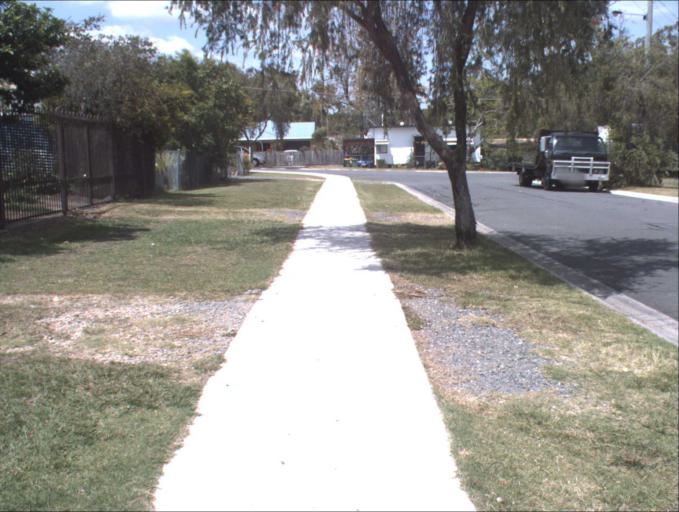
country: AU
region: Queensland
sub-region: Logan
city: Woodridge
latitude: -27.6334
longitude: 153.0961
